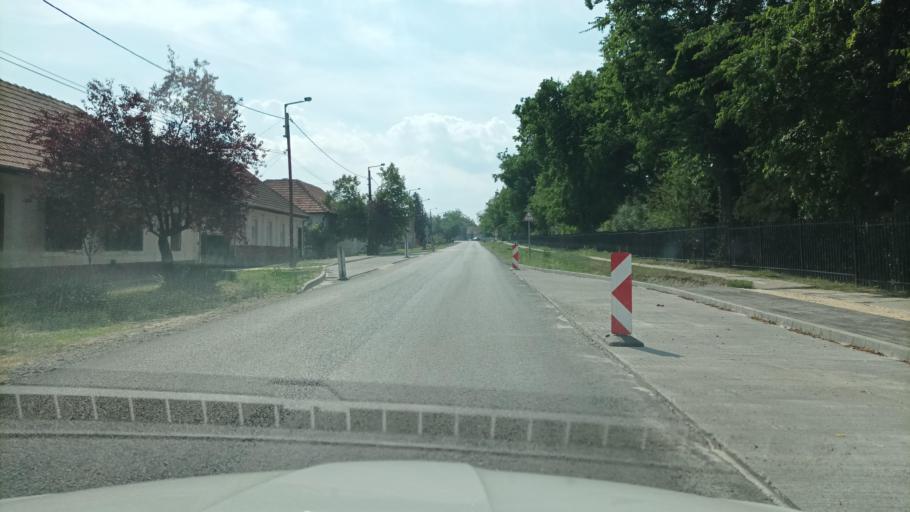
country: HU
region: Pest
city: Tura
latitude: 47.6034
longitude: 19.6046
